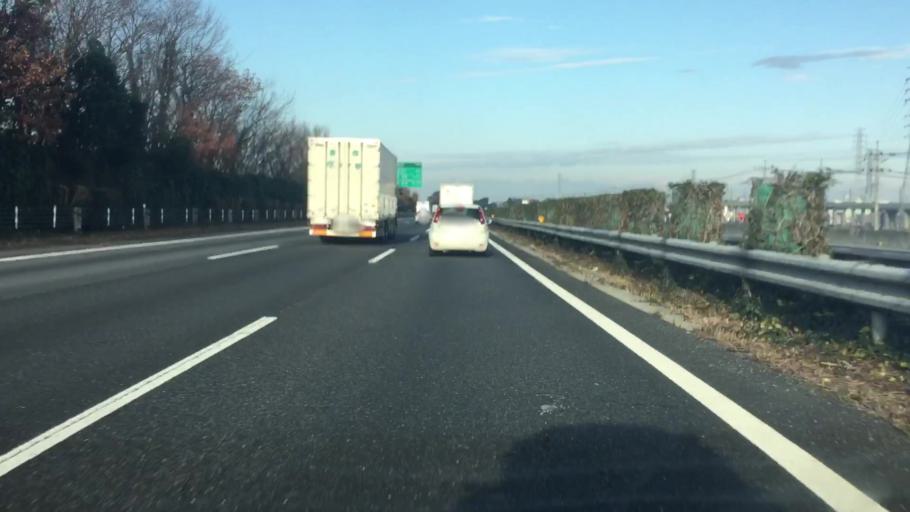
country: JP
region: Saitama
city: Honjo
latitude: 36.2267
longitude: 139.1561
